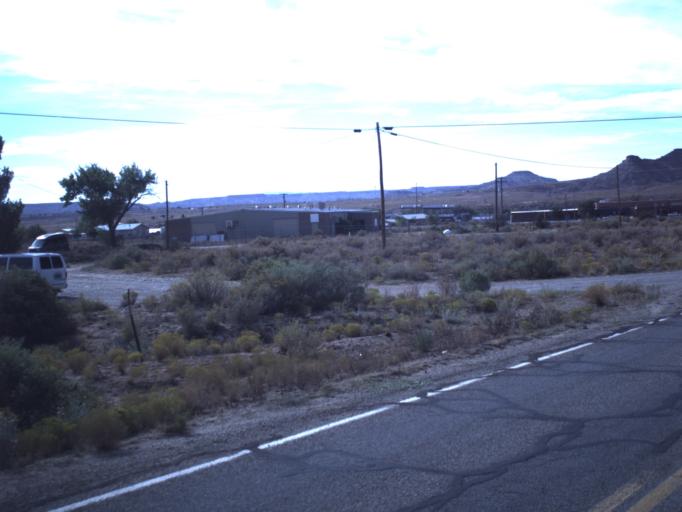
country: US
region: Utah
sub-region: San Juan County
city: Blanding
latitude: 37.2646
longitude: -109.3044
